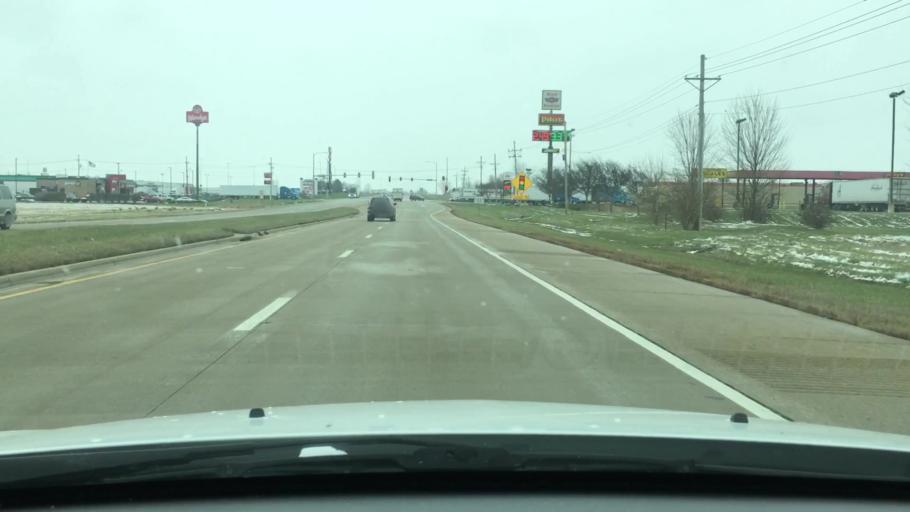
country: US
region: Illinois
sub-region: Ogle County
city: Hillcrest
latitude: 41.9343
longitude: -89.0375
